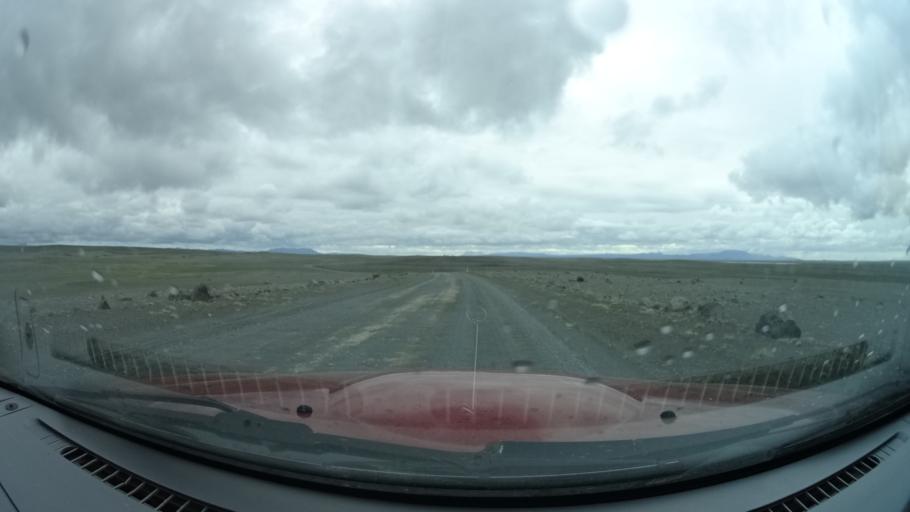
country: IS
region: Northeast
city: Laugar
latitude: 65.7247
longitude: -16.3322
